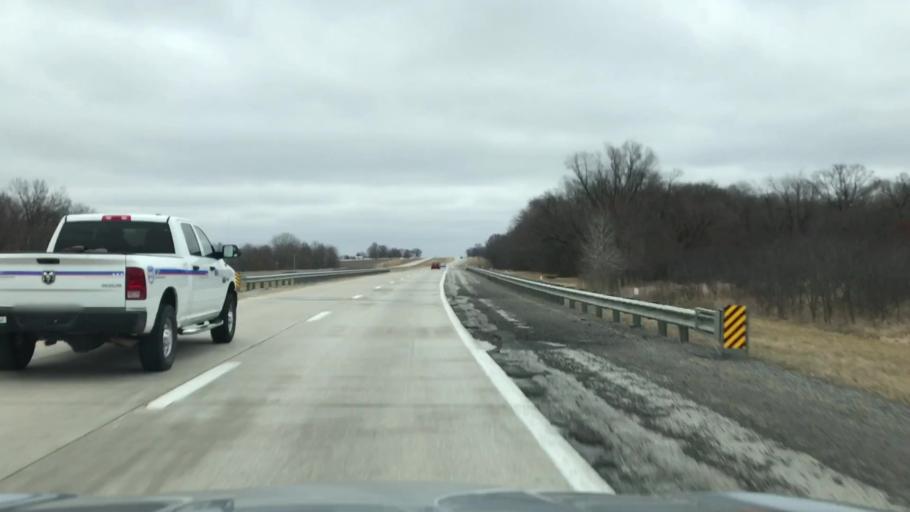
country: US
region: Missouri
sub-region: Livingston County
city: Chillicothe
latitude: 39.7773
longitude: -93.3618
